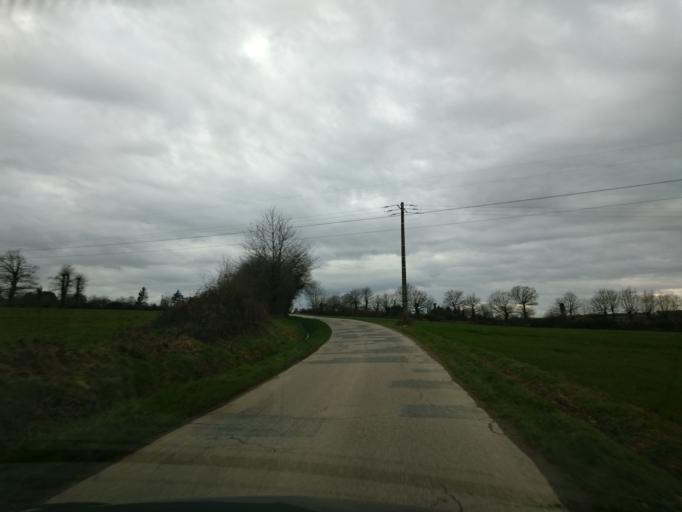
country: FR
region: Brittany
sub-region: Departement d'Ille-et-Vilaine
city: Crevin
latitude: 47.9217
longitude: -1.6353
